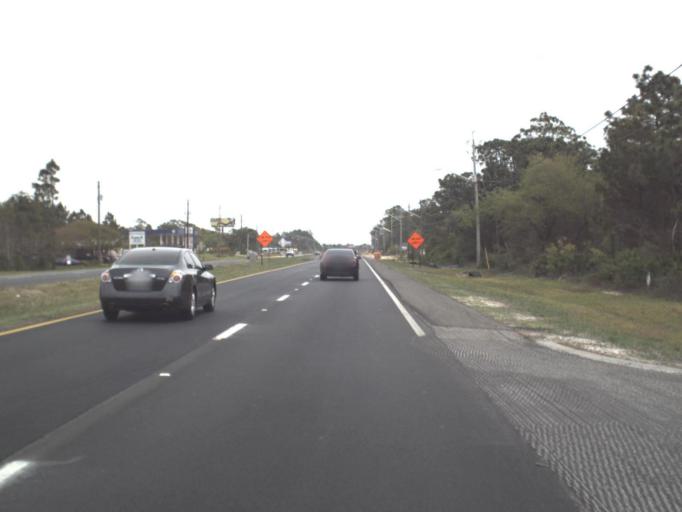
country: US
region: Florida
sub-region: Santa Rosa County
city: Woodlawn Beach
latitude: 30.4038
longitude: -86.9691
